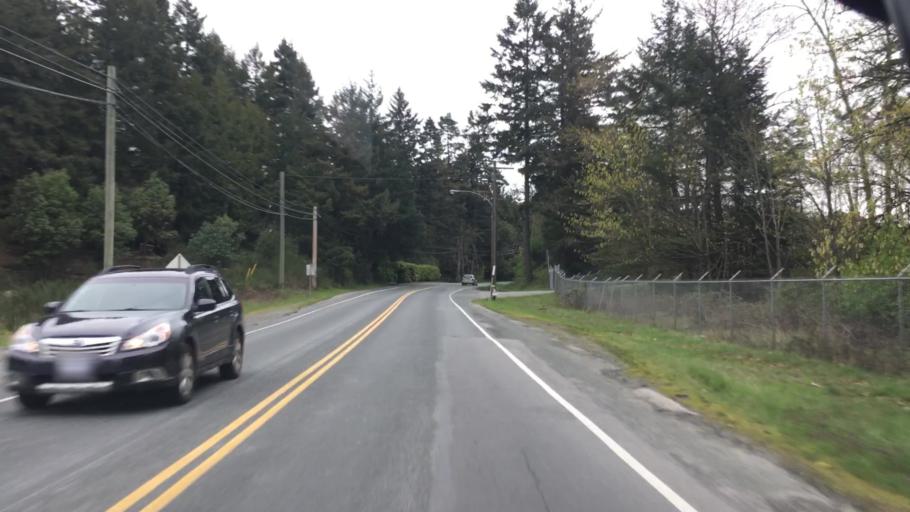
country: CA
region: British Columbia
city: North Saanich
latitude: 48.5655
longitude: -123.4271
